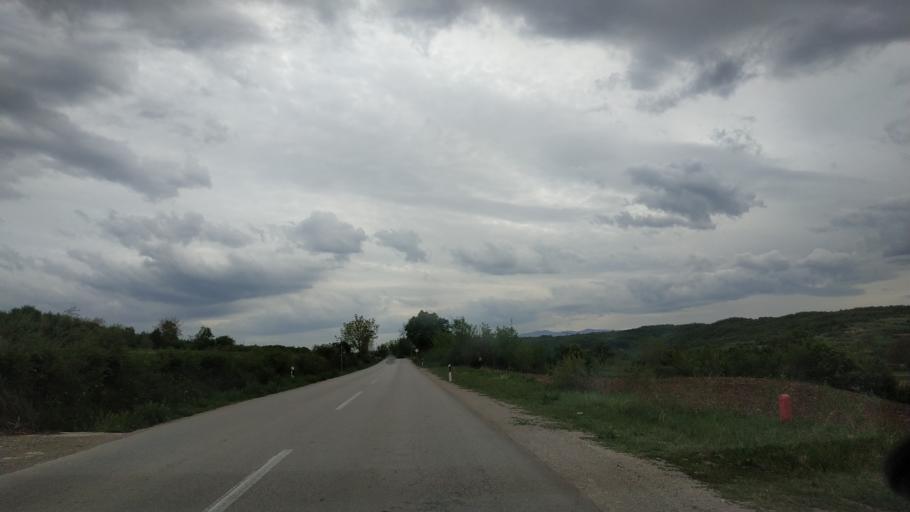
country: RS
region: Central Serbia
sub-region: Nisavski Okrug
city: Aleksinac
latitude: 43.6194
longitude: 21.6922
